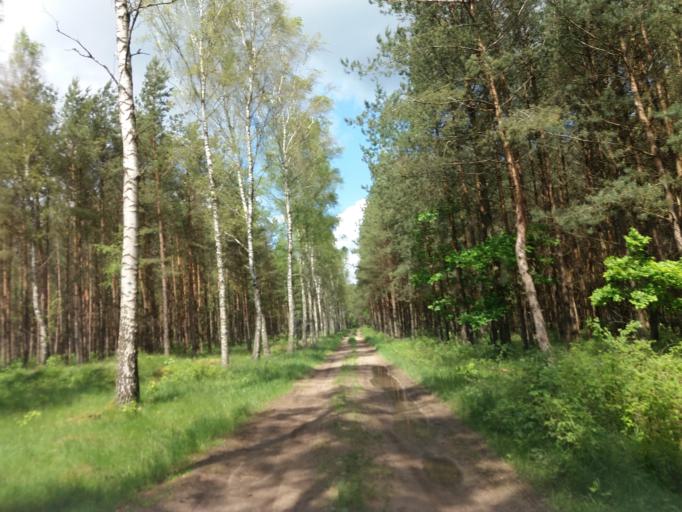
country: PL
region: West Pomeranian Voivodeship
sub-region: Powiat choszczenski
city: Drawno
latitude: 53.2604
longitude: 15.7463
